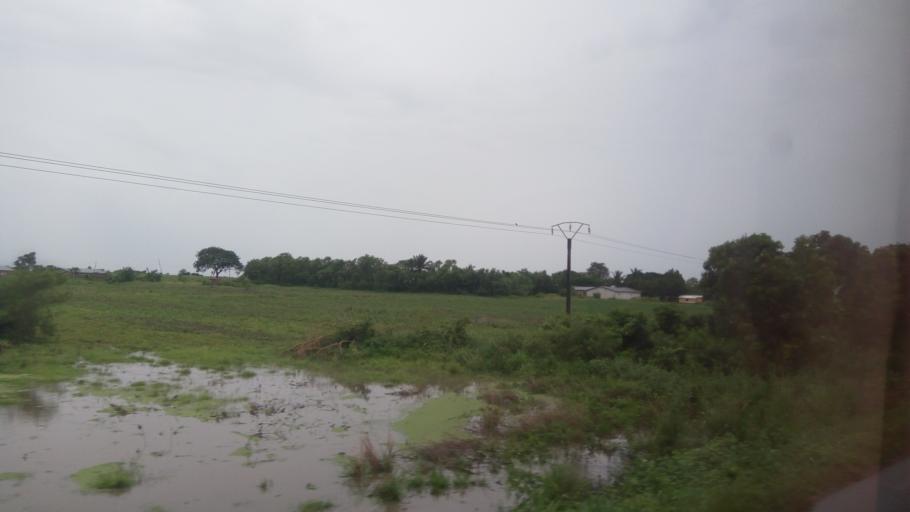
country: TG
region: Plateaux
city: Notse
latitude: 7.0998
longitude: 1.1558
